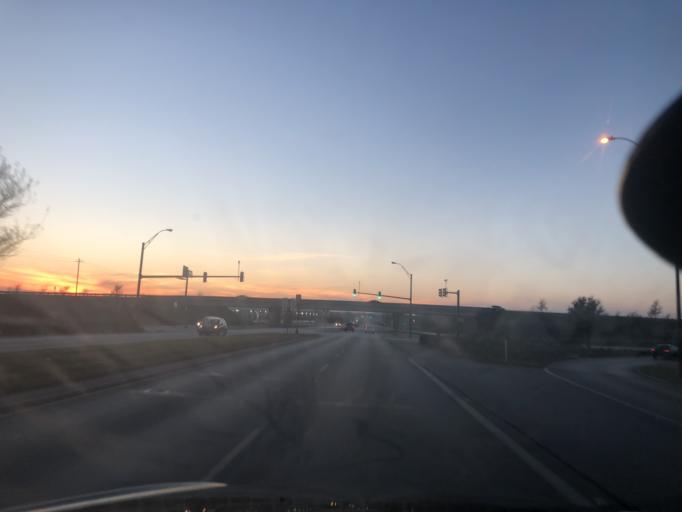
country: US
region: Texas
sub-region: Tarrant County
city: White Settlement
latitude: 32.7246
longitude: -97.4784
